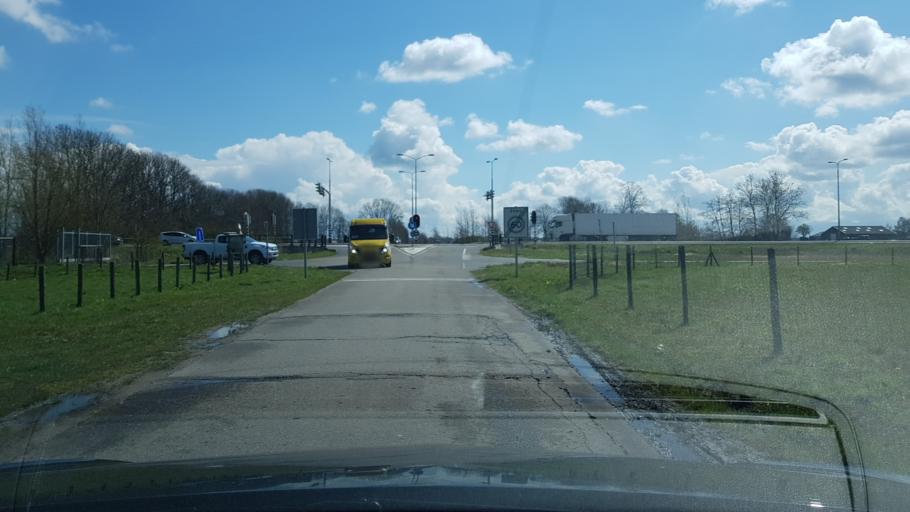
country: NL
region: North Holland
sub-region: Gemeente Uithoorn
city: Uithoorn
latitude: 52.2357
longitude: 4.8524
